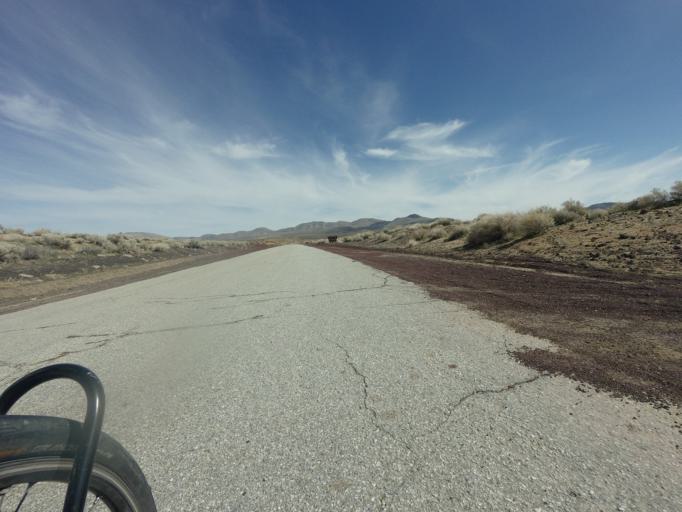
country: US
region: California
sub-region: Kern County
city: Inyokern
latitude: 35.9770
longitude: -117.9197
